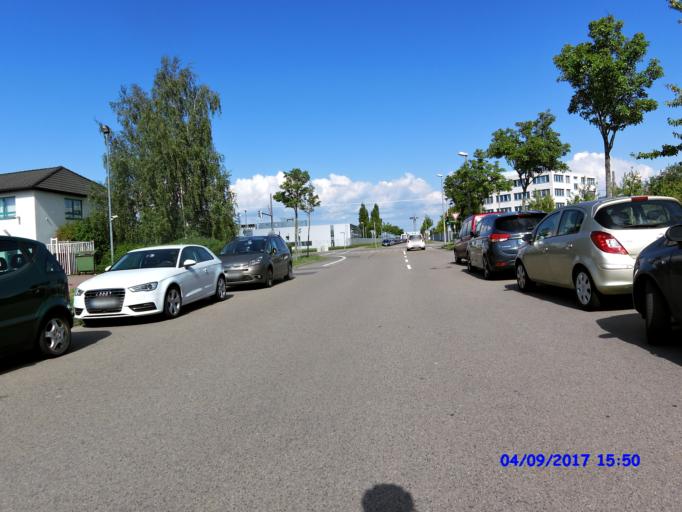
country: DE
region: Saxony
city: Taucha
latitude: 51.3640
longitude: 12.4644
